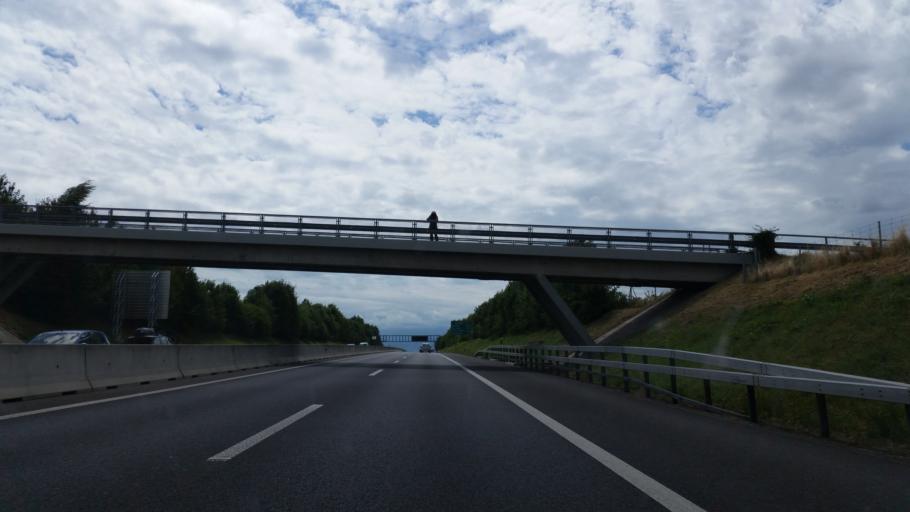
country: CH
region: Vaud
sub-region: Gros-de-Vaud District
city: Penthalaz
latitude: 46.5894
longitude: 6.5541
